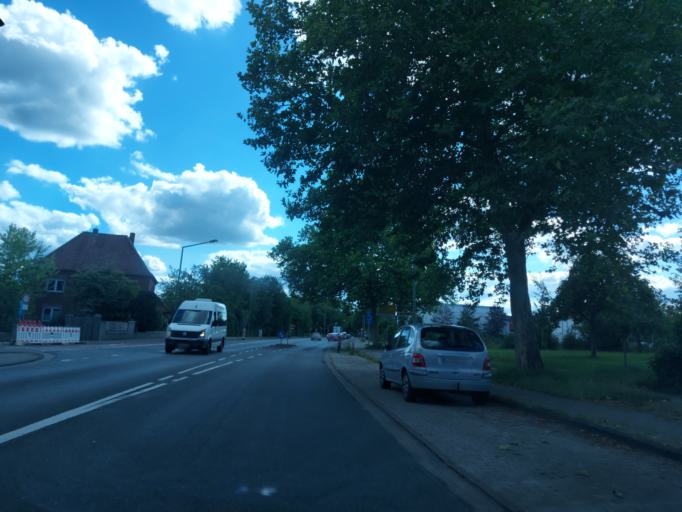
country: DE
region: Lower Saxony
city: Georgsmarienhutte
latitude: 52.2376
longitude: 8.0291
